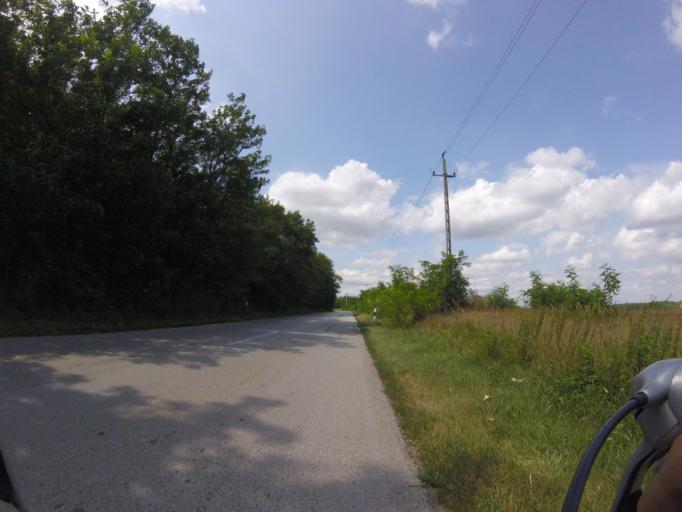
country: HU
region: Szabolcs-Szatmar-Bereg
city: Kemecse
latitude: 48.0626
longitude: 21.8418
